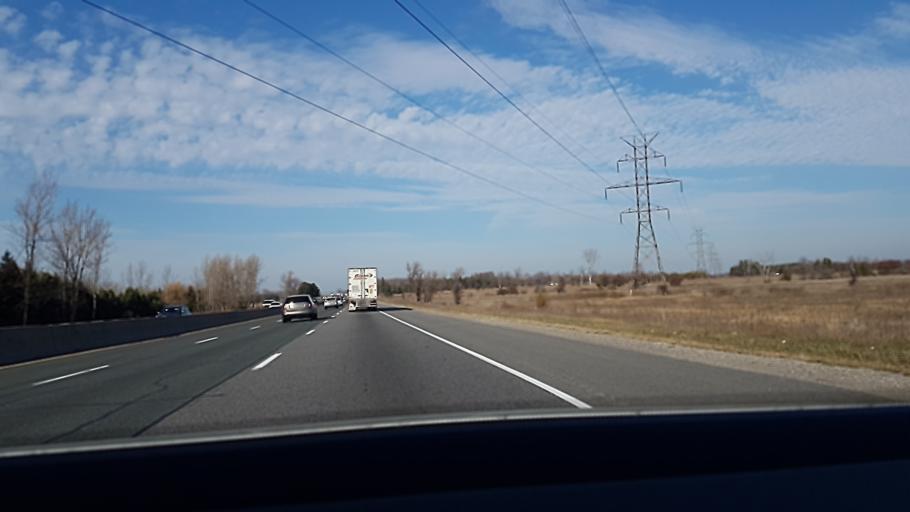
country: CA
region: Ontario
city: Newmarket
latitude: 43.9867
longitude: -79.5817
